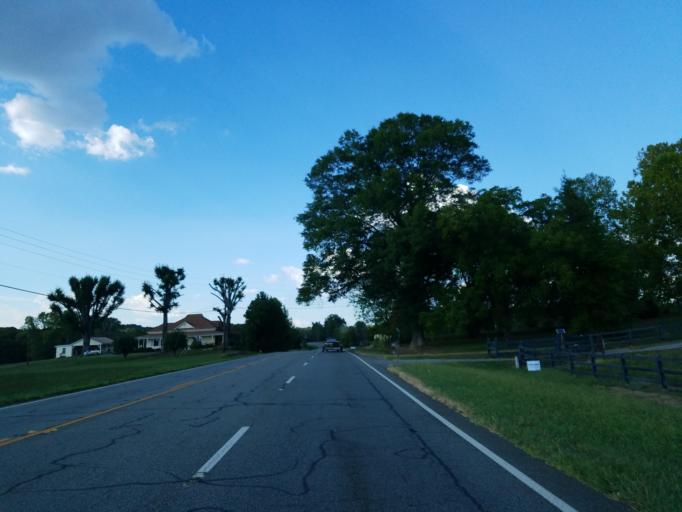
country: US
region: Georgia
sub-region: Bartow County
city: Rydal
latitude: 34.5362
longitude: -84.7063
